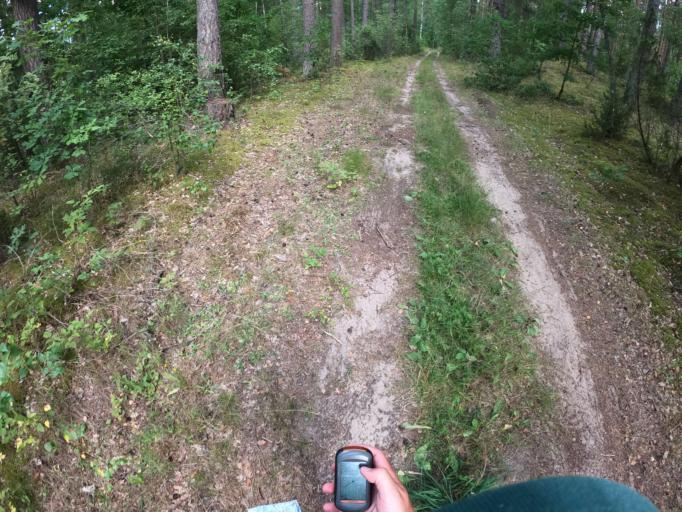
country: LT
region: Alytaus apskritis
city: Druskininkai
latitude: 54.1324
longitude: 24.1576
